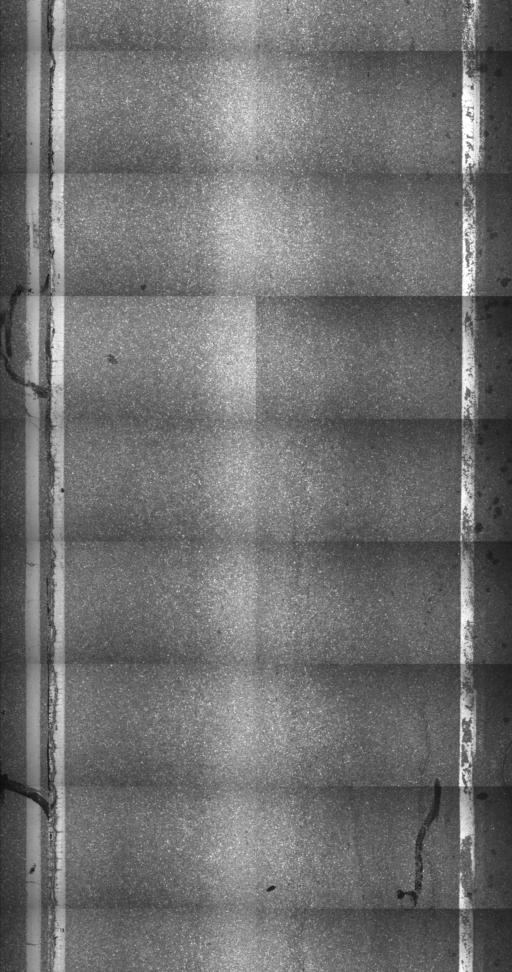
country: US
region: Vermont
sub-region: Franklin County
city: Saint Albans
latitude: 44.7323
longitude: -73.0470
